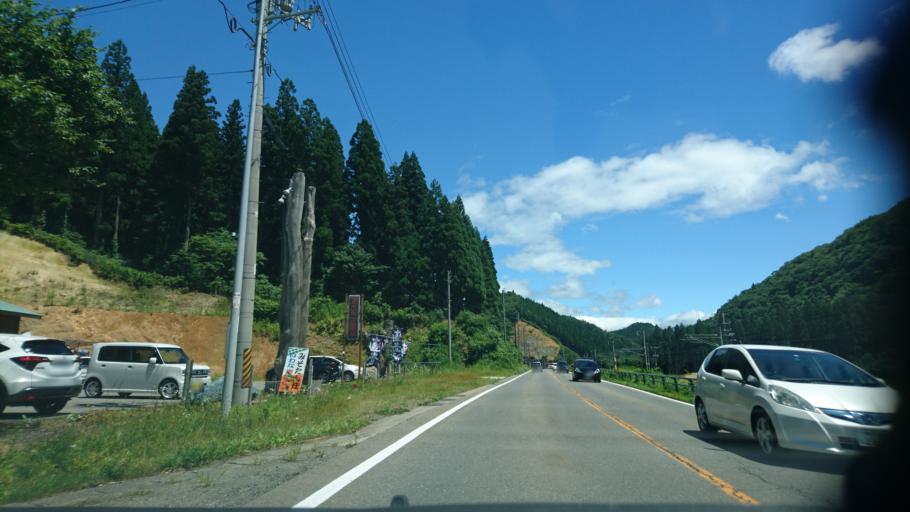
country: JP
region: Akita
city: Kakunodatemachi
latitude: 39.6477
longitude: 140.6650
